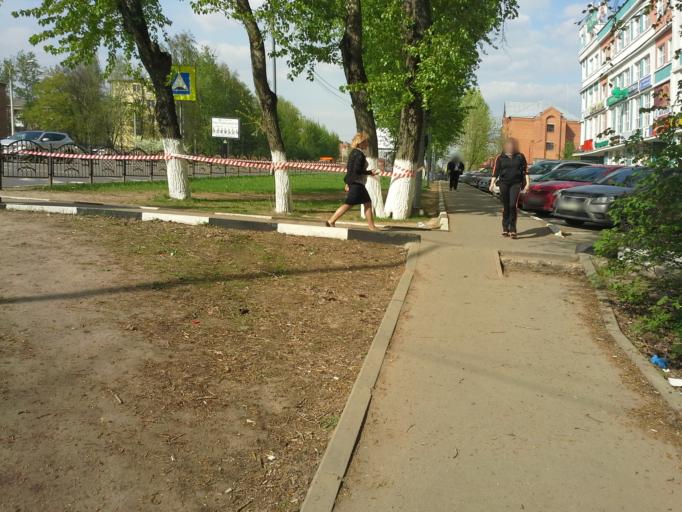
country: RU
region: Moskovskaya
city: Sergiyev Posad
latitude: 56.3221
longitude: 38.1448
